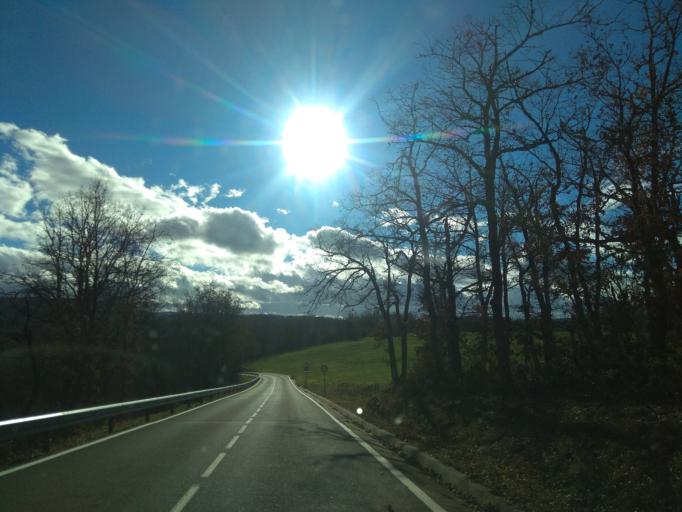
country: ES
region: Cantabria
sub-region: Provincia de Cantabria
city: San Martin de Elines
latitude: 42.9052
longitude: -3.8680
